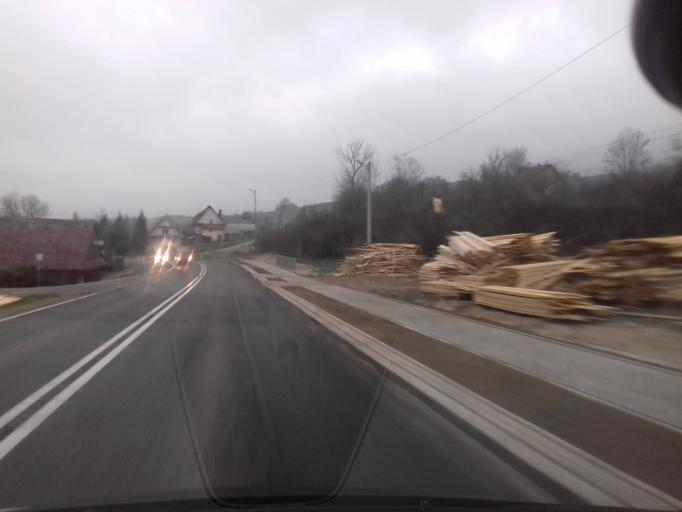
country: PL
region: Lesser Poland Voivodeship
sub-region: Powiat limanowski
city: Kasina Wielka
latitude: 49.6969
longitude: 20.1239
